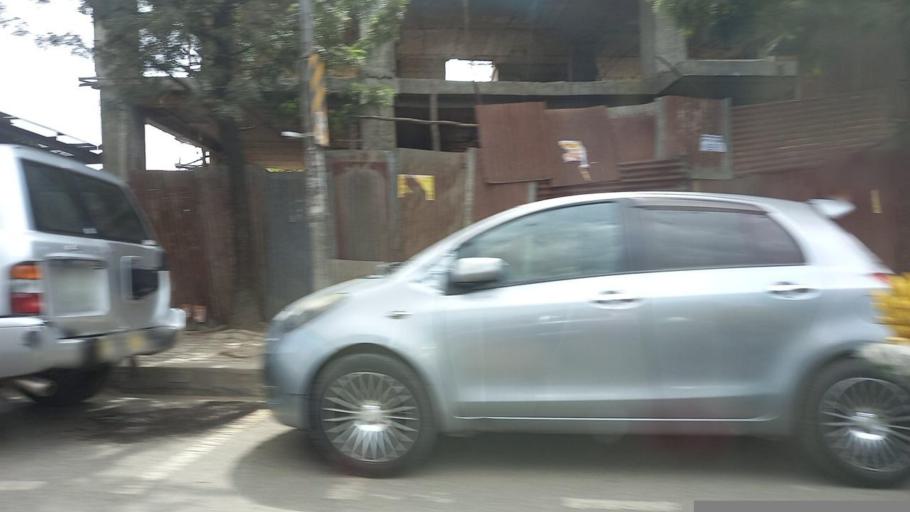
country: ET
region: Adis Abeba
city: Addis Ababa
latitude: 9.0218
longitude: 38.7881
